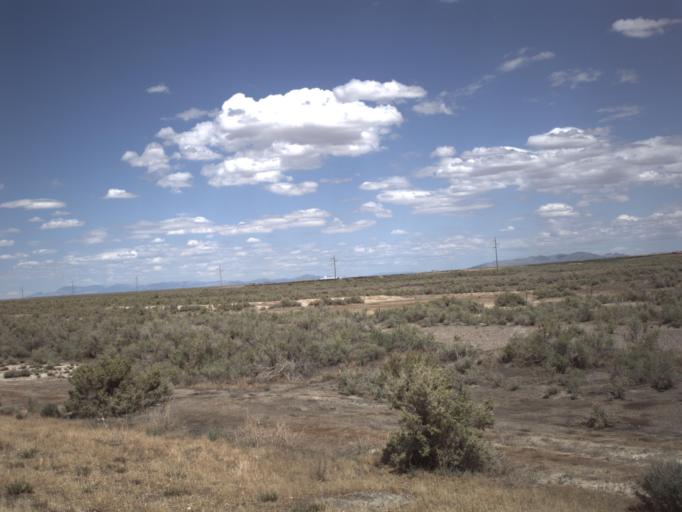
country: US
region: Utah
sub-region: Millard County
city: Delta
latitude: 39.2581
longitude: -112.4443
